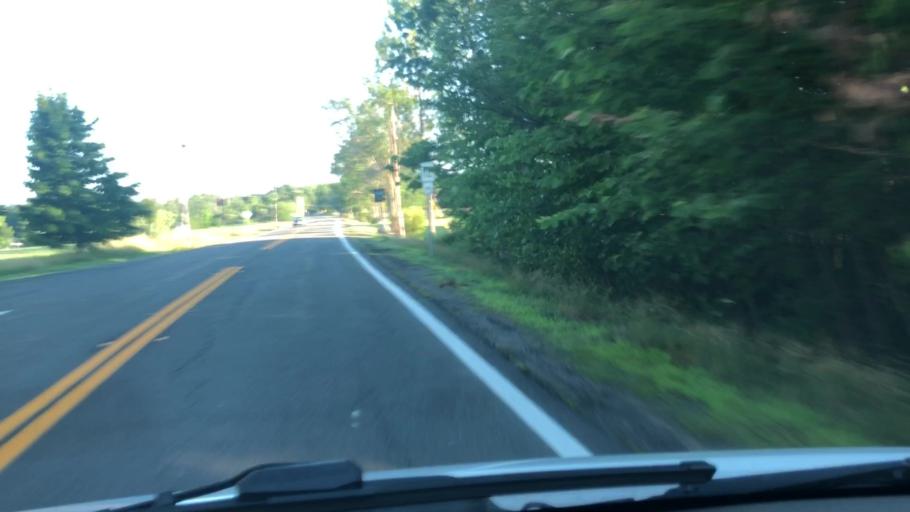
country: US
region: Massachusetts
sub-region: Hampshire County
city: Chesterfield
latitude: 42.3793
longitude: -72.9230
